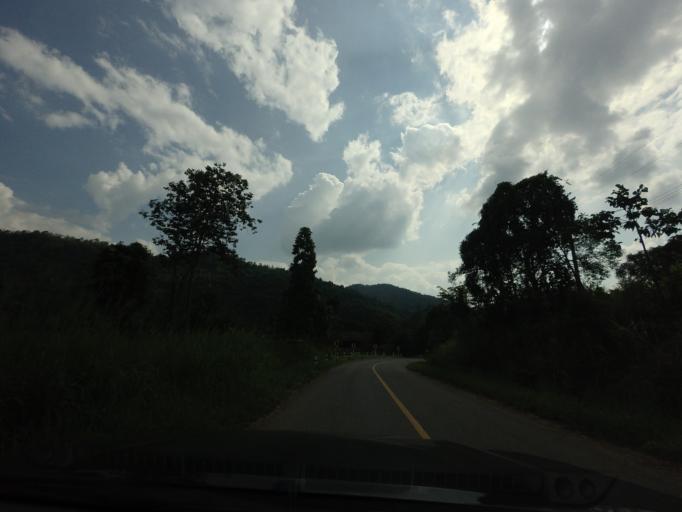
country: TH
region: Uttaradit
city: Ban Khok
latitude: 18.2313
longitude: 101.0274
